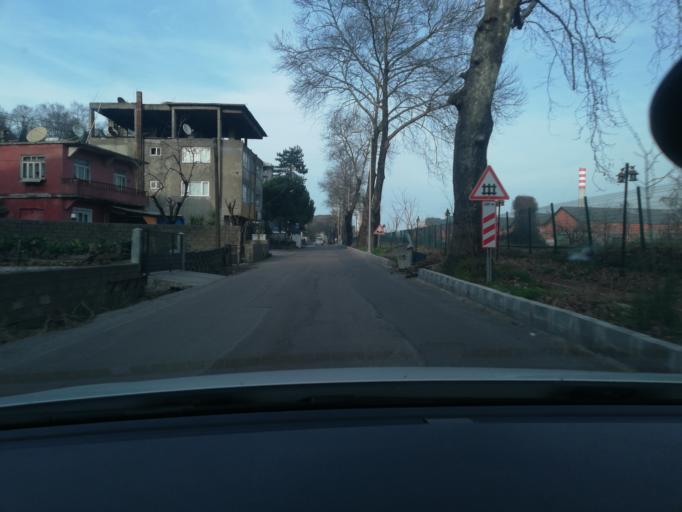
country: TR
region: Zonguldak
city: Kilimli
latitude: 41.5091
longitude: 31.8889
